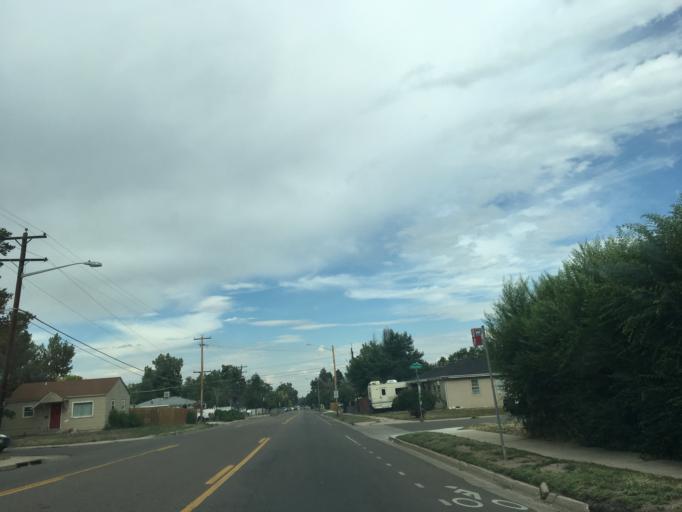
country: US
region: Colorado
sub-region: Arapahoe County
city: Sheridan
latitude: 39.6894
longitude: -105.0383
